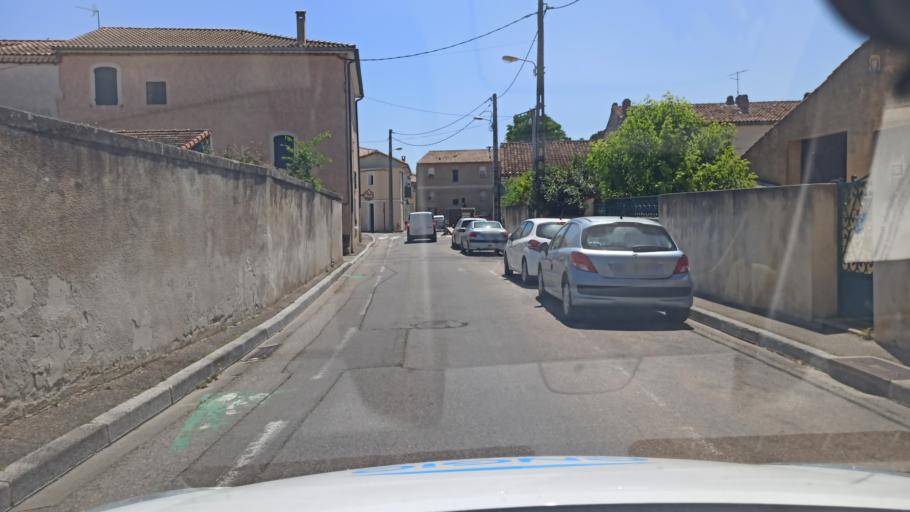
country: FR
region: Provence-Alpes-Cote d'Azur
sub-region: Departement du Vaucluse
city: Morieres-les-Avignon
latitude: 43.9400
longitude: 4.9054
